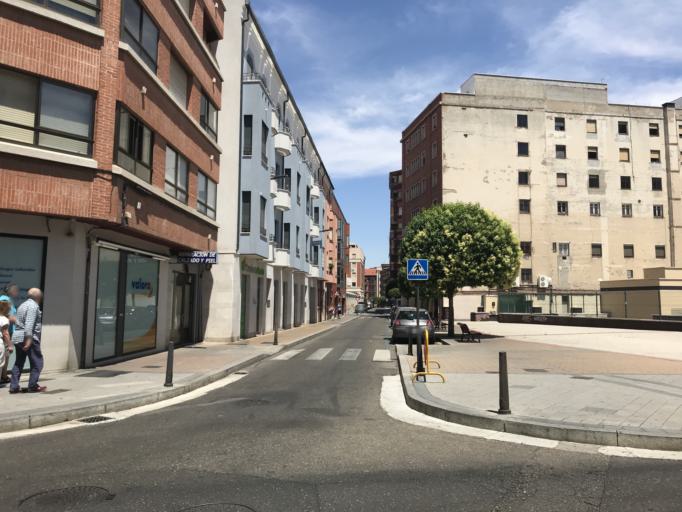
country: ES
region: Castille and Leon
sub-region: Provincia de Valladolid
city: Valladolid
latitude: 41.6492
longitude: -4.7231
